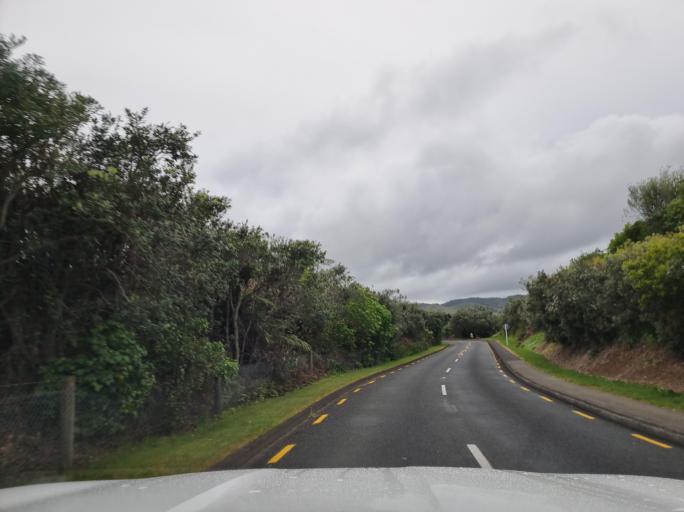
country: NZ
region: Northland
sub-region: Whangarei
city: Whangarei
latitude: -35.7691
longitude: 174.3688
